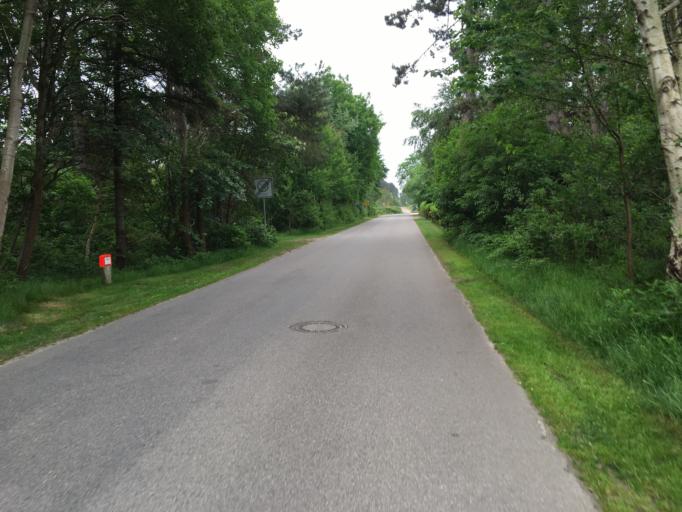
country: DE
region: Schleswig-Holstein
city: Norddorf
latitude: 54.6719
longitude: 8.3347
